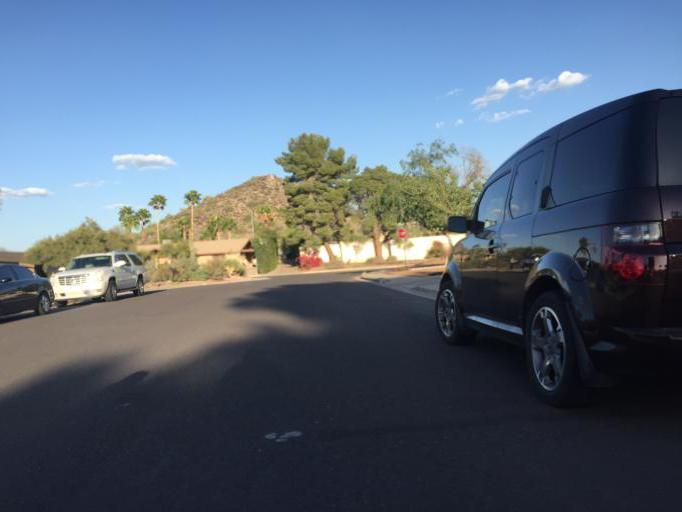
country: US
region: Arizona
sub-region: Maricopa County
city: Paradise Valley
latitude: 33.5721
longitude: -112.0060
